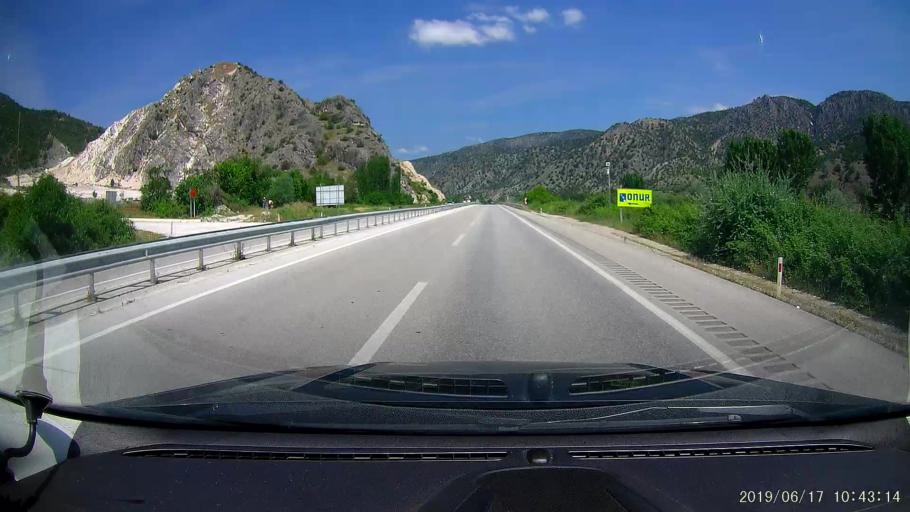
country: TR
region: Corum
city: Kargi
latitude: 41.0609
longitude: 34.5393
